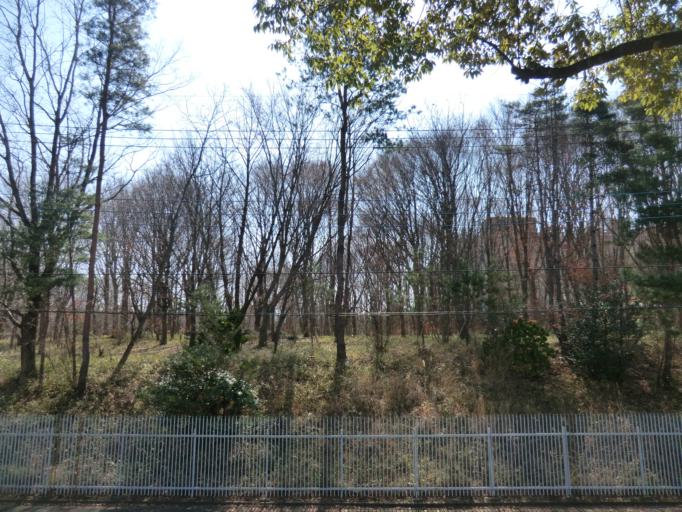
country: JP
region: Ibaraki
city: Naka
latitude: 36.1037
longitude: 140.1113
